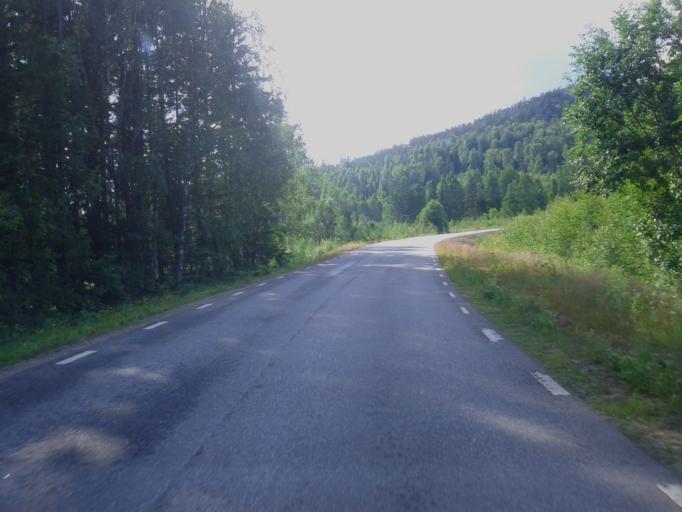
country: SE
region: Vaesternorrland
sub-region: Kramfors Kommun
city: Nordingra
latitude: 63.0651
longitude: 18.3614
